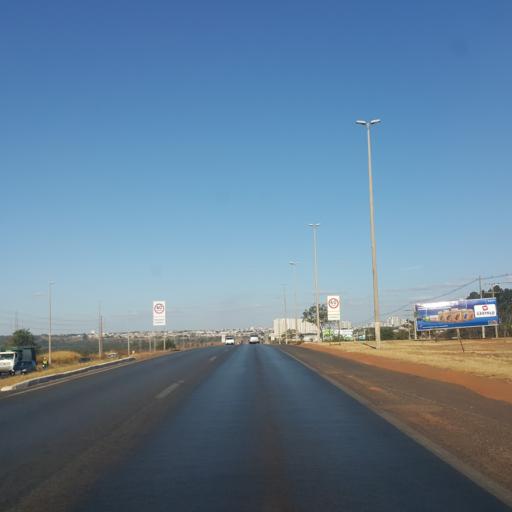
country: BR
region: Federal District
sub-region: Brasilia
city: Brasilia
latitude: -15.7879
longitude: -48.1144
